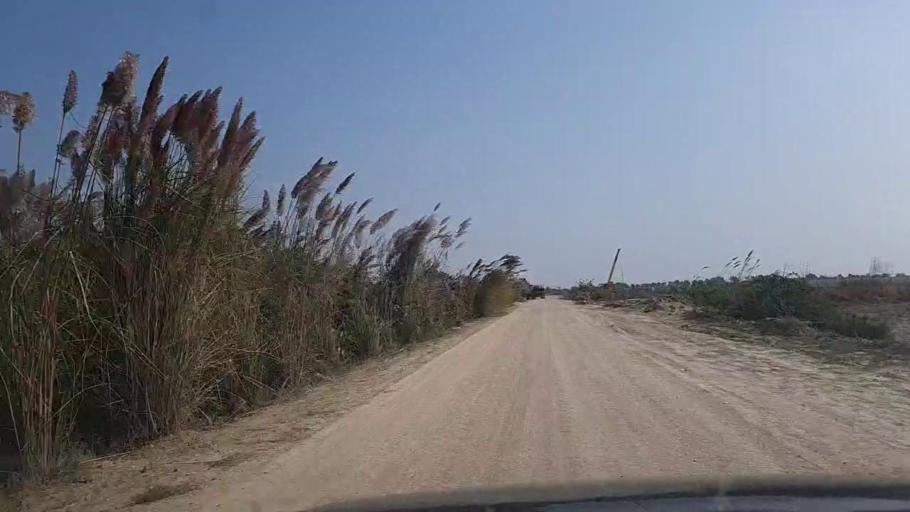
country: PK
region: Sindh
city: Gharo
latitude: 24.7186
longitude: 67.5630
